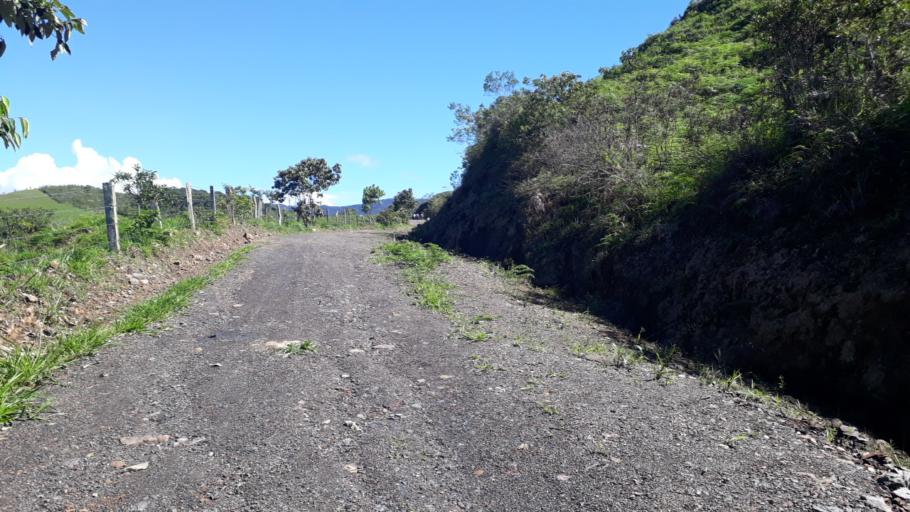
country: CO
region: Casanare
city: Nunchia
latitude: 5.6685
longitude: -72.4294
